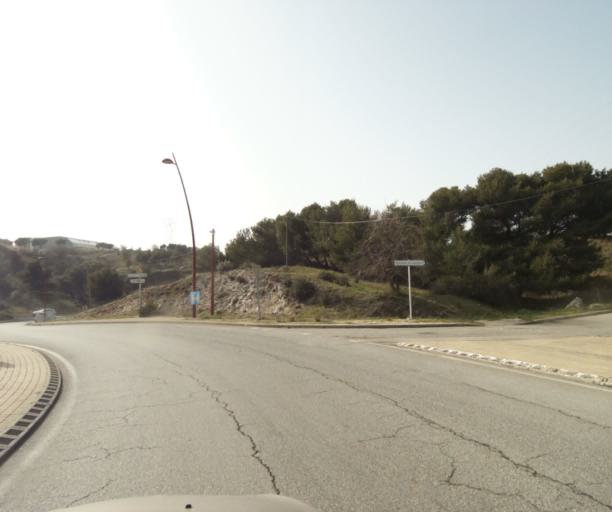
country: FR
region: Provence-Alpes-Cote d'Azur
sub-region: Departement des Bouches-du-Rhone
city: Les Pennes-Mirabeau
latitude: 43.4020
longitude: 5.3351
